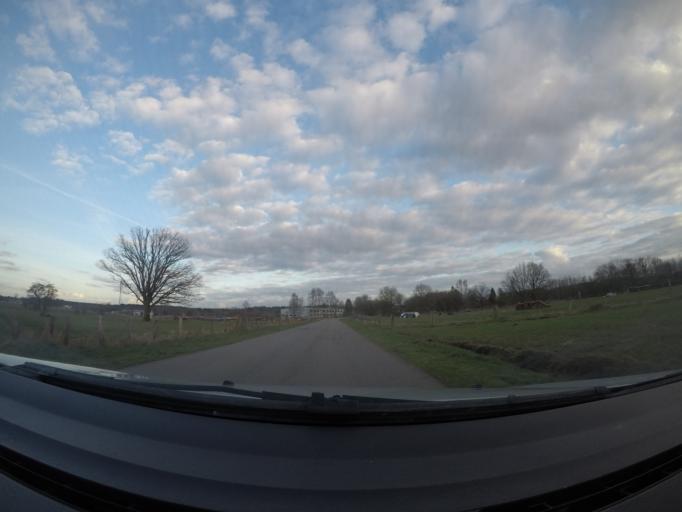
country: BE
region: Wallonia
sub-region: Province du Luxembourg
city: Etalle
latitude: 49.6689
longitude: 5.5683
